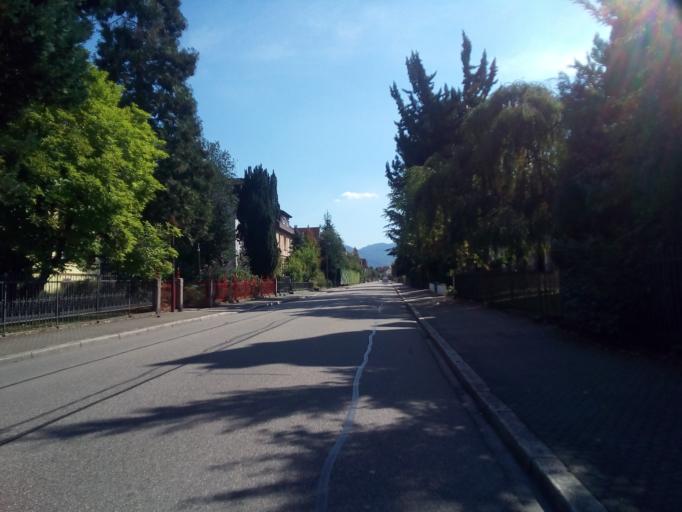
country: DE
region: Baden-Wuerttemberg
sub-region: Freiburg Region
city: Achern
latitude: 48.6251
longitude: 8.0764
